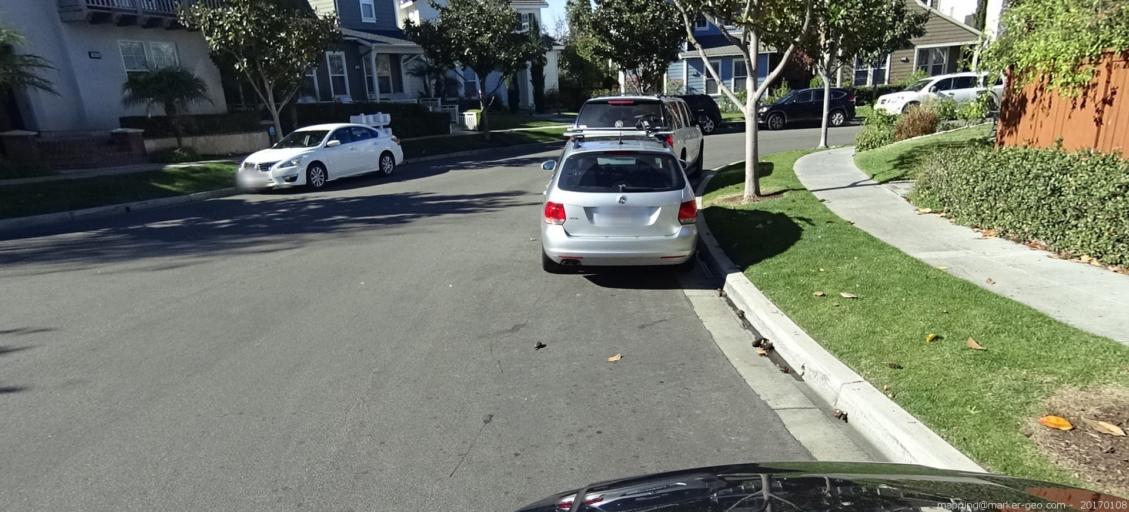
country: US
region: California
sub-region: Orange County
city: Ladera Ranch
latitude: 33.5595
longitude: -117.6458
